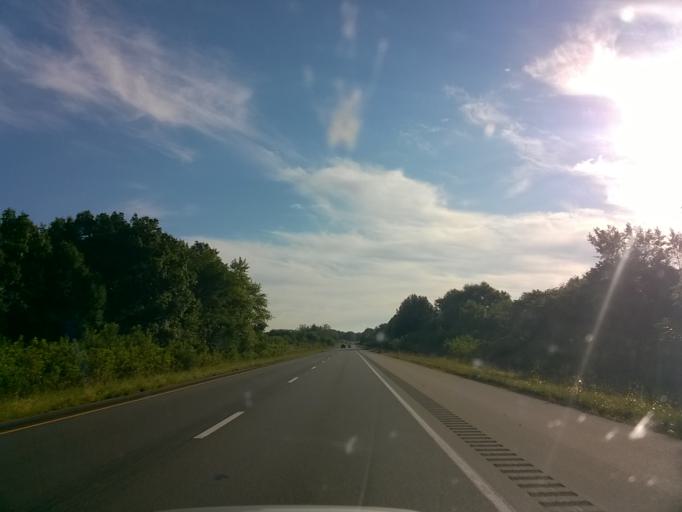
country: US
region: Indiana
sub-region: Warrick County
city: Chandler
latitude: 38.1797
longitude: -87.4007
